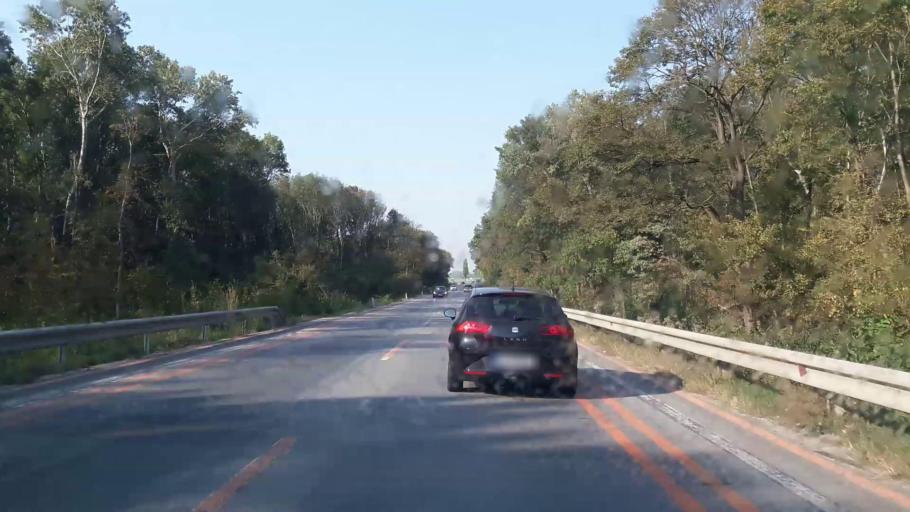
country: AT
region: Lower Austria
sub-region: Politischer Bezirk Ganserndorf
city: Engelhartstetten
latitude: 48.1581
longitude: 16.9000
